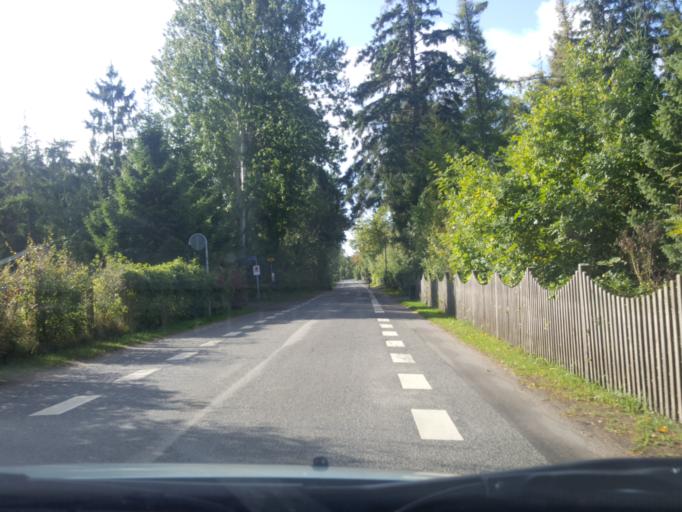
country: DK
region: Zealand
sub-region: Guldborgsund Kommune
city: Nykobing Falster
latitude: 54.6851
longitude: 11.9637
